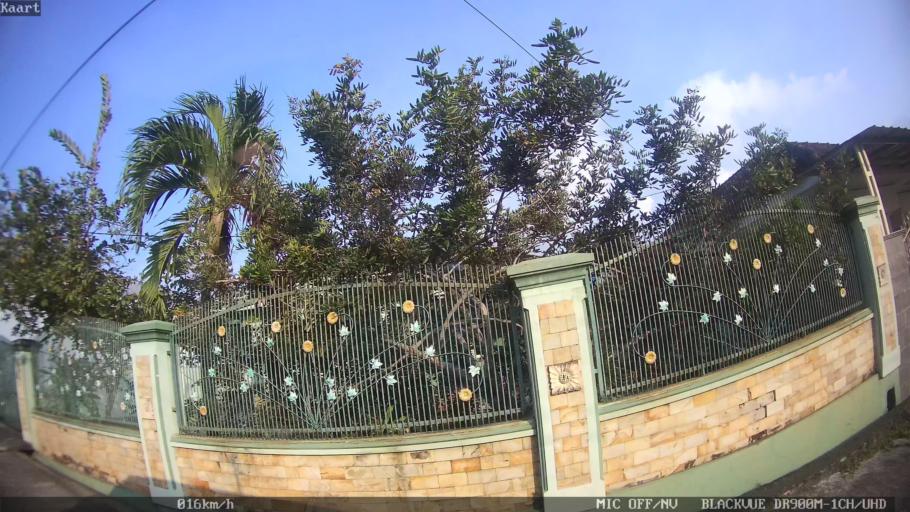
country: ID
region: Lampung
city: Kedaton
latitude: -5.3991
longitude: 105.2987
